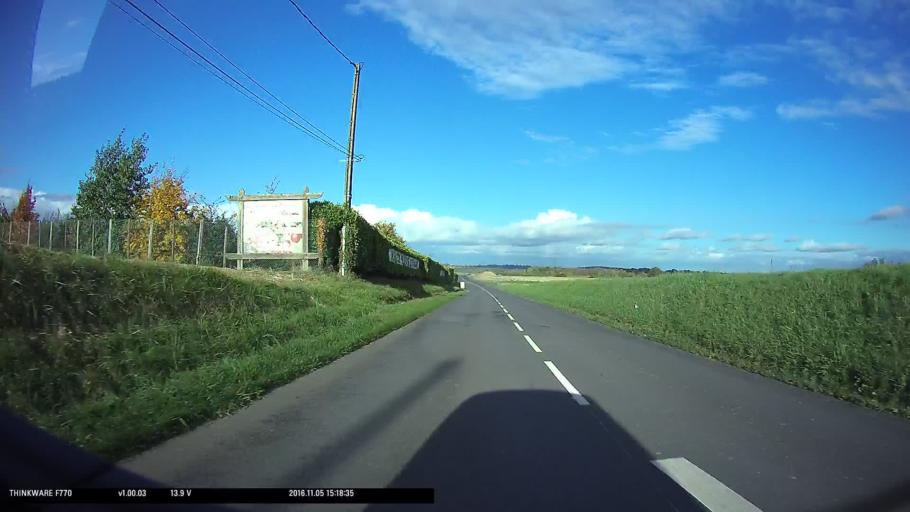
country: FR
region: Ile-de-France
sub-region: Departement du Val-d'Oise
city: Ableiges
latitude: 49.0750
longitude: 1.9699
